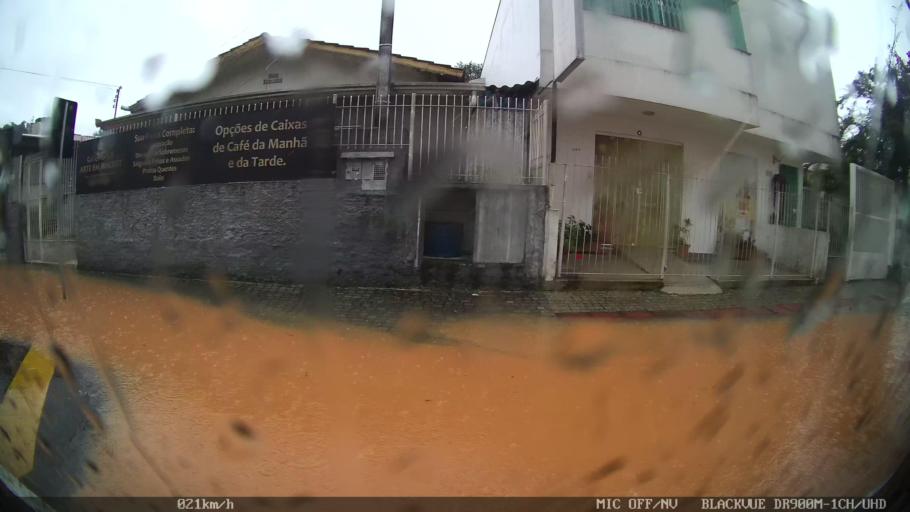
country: BR
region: Santa Catarina
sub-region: Balneario Camboriu
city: Balneario Camboriu
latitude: -26.9894
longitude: -48.6406
